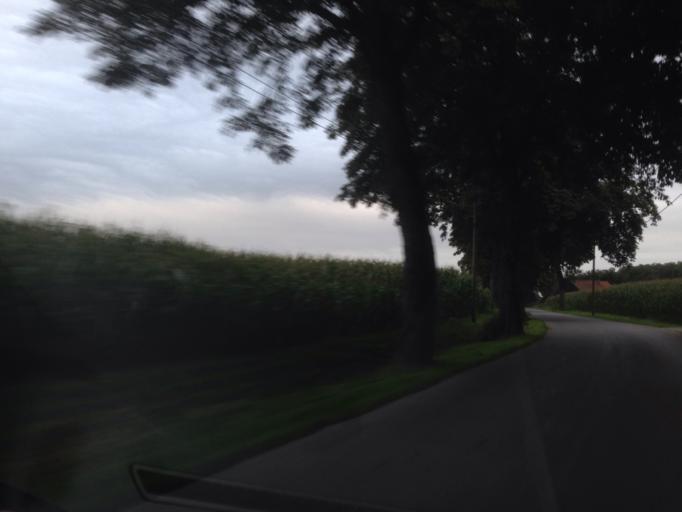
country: DE
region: North Rhine-Westphalia
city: Olfen
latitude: 51.7421
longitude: 7.4062
